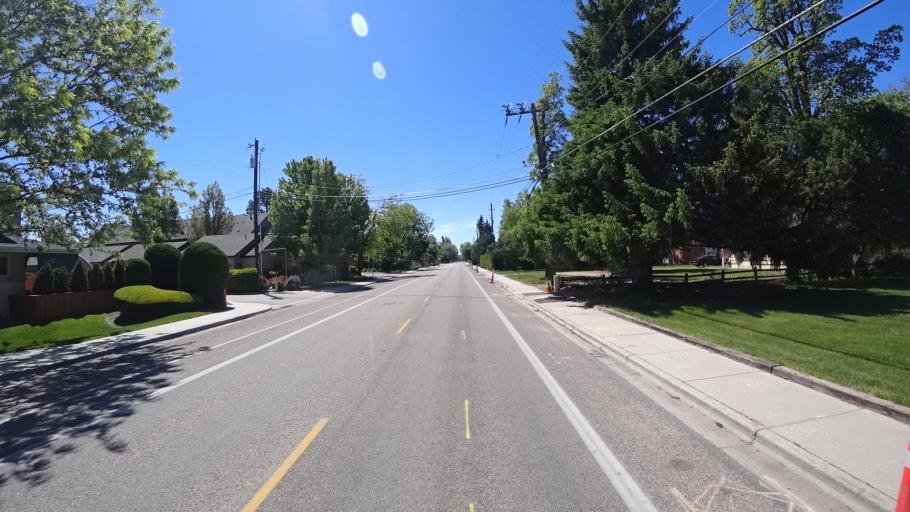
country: US
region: Idaho
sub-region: Ada County
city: Boise
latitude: 43.5835
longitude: -116.1836
